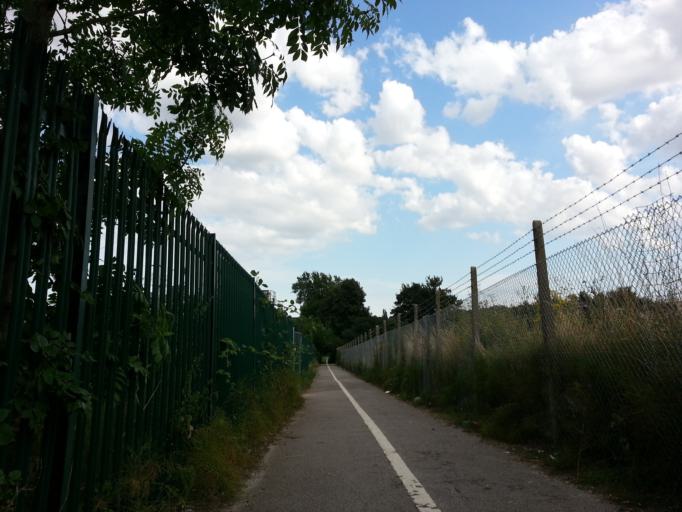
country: GB
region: England
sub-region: Suffolk
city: Ipswich
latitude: 52.0551
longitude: 1.1309
